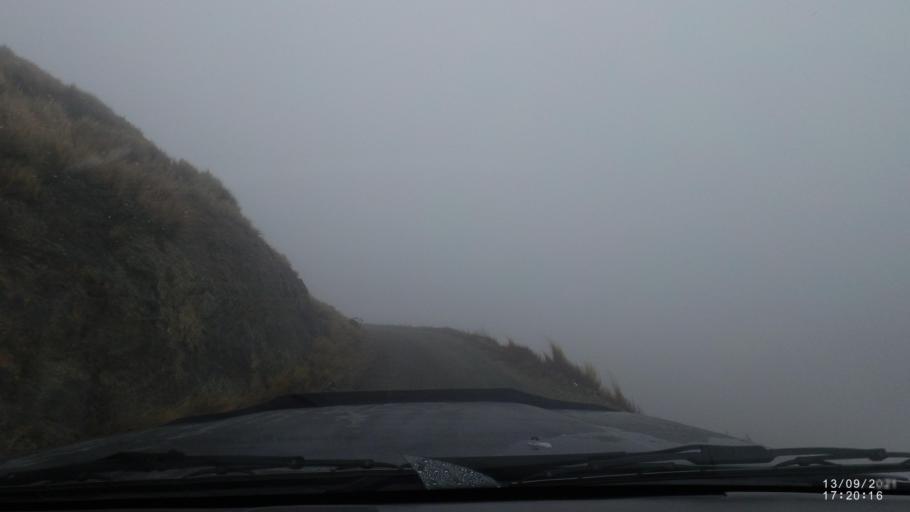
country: BO
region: Cochabamba
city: Colomi
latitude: -17.3510
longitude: -65.7657
